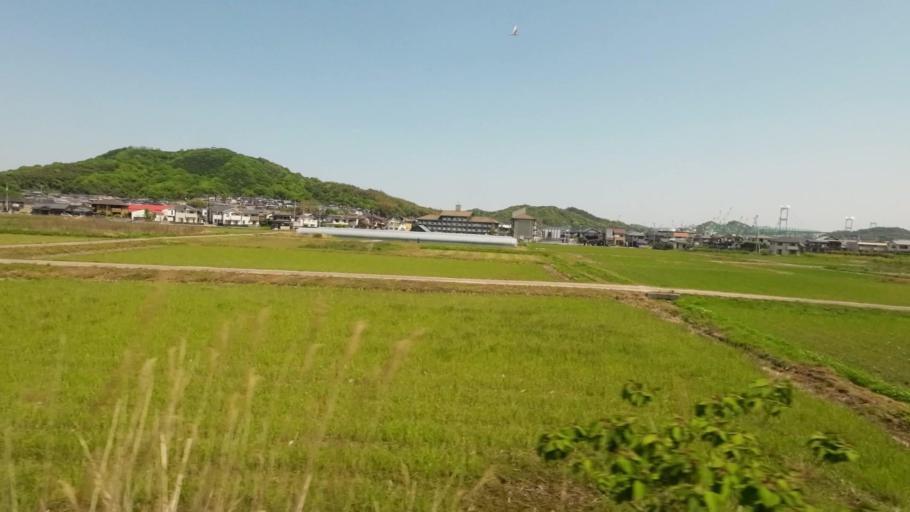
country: JP
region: Ehime
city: Hojo
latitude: 34.0955
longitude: 132.9565
